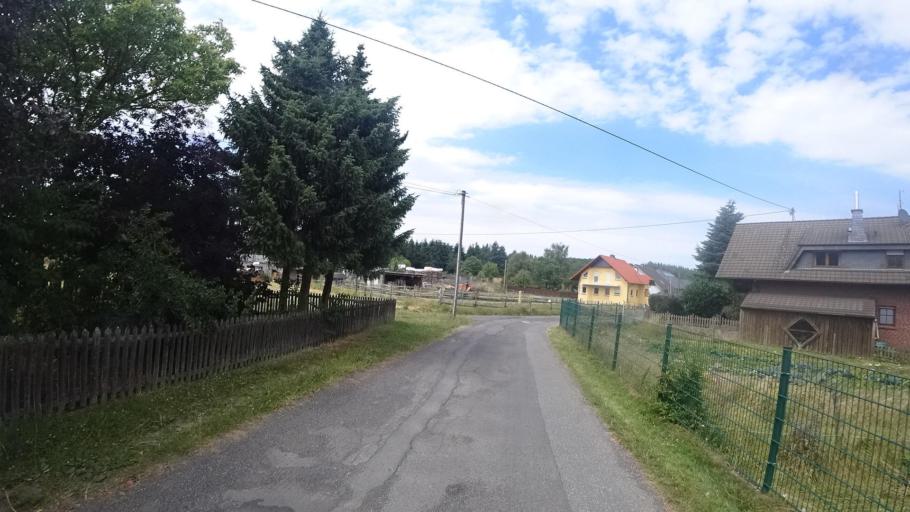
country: DE
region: Rheinland-Pfalz
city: Spessart
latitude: 50.4892
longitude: 7.0938
